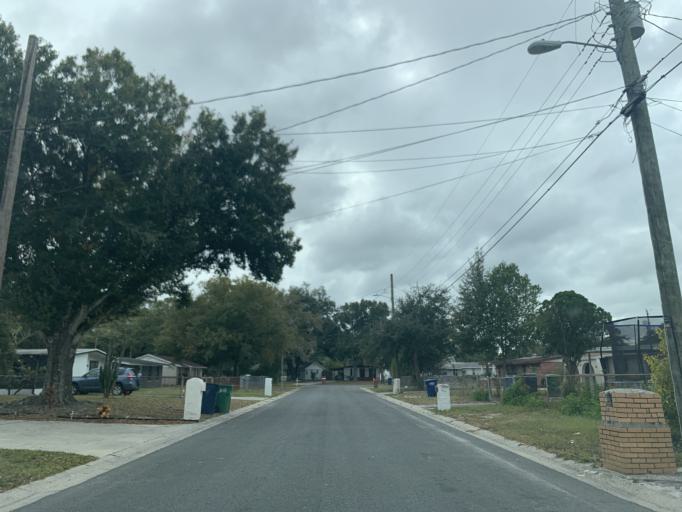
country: US
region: Florida
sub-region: Hillsborough County
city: East Lake-Orient Park
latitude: 27.9732
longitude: -82.4052
